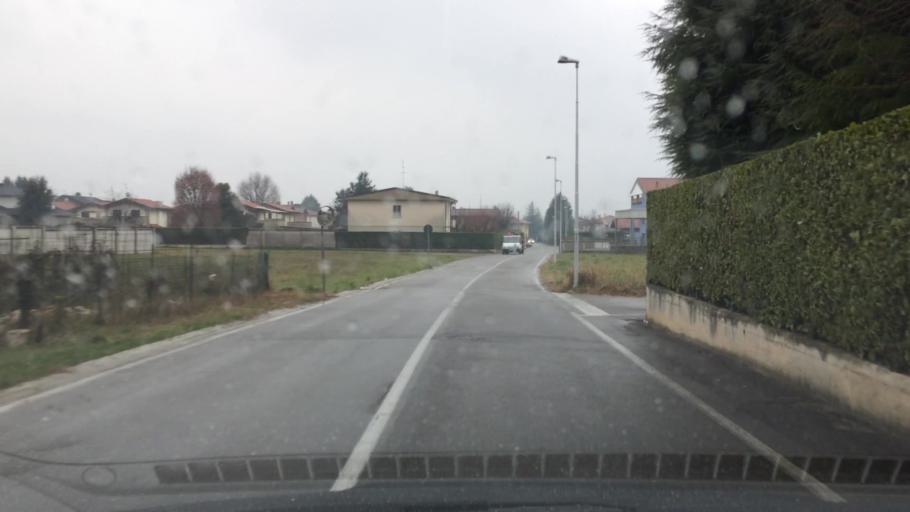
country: IT
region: Lombardy
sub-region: Provincia di Como
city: San Michele-San Giorgio
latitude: 45.6949
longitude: 9.0568
